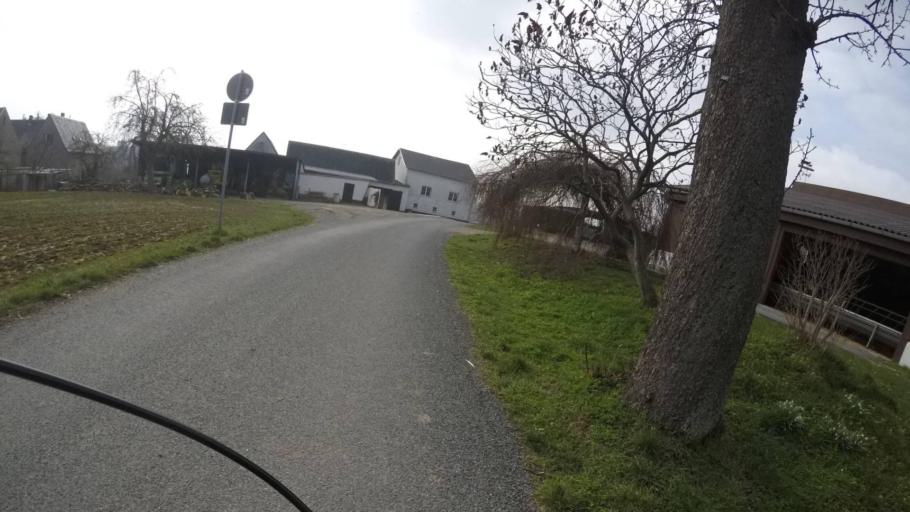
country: DE
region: Saxony
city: Niederfrohna
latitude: 50.8731
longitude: 12.6957
